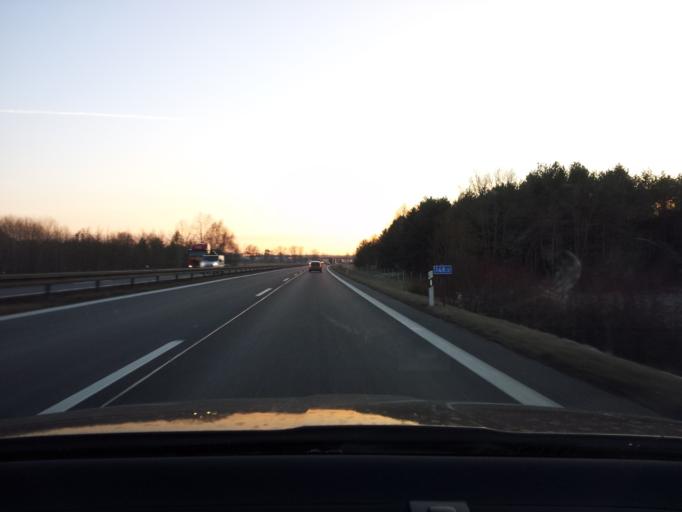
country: DE
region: Brandenburg
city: Brieselang
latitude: 52.6552
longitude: 13.0024
